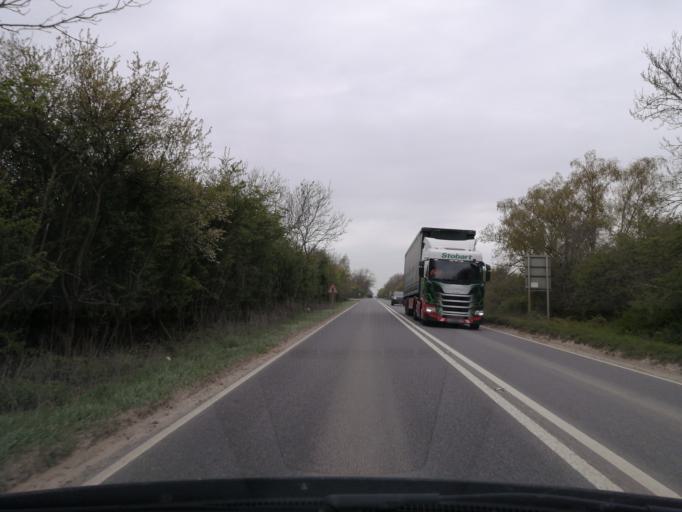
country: GB
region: England
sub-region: Peterborough
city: Wittering
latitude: 52.5899
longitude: -0.4481
